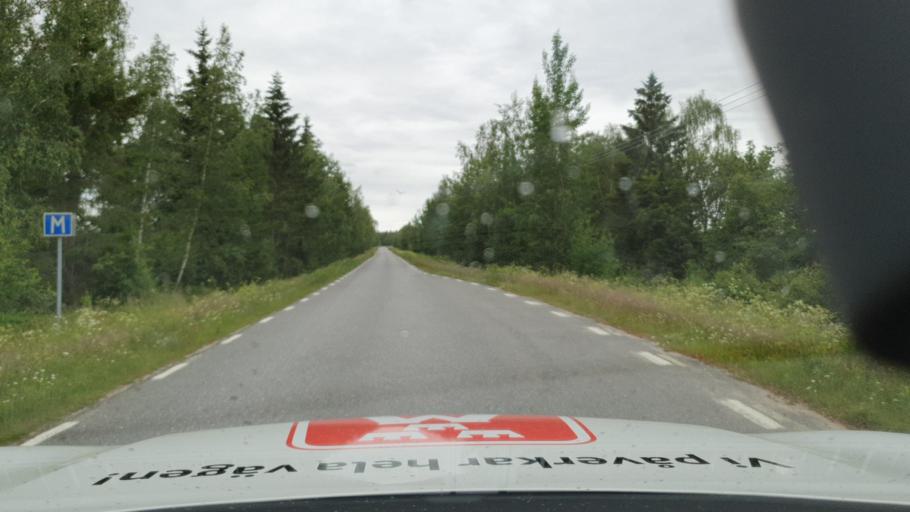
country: SE
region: Vaesterbotten
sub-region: Nordmalings Kommun
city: Nordmaling
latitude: 63.4640
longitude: 19.4655
